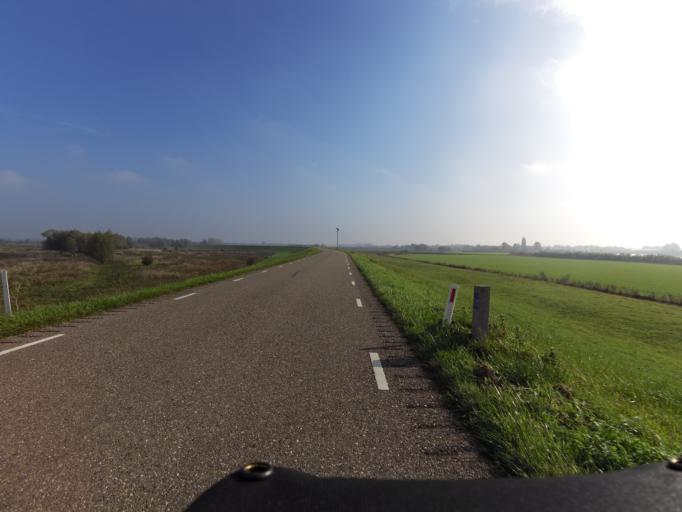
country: NL
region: Gelderland
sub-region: Gemeente Groesbeek
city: Berg en Dal
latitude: 51.8493
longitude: 5.9728
